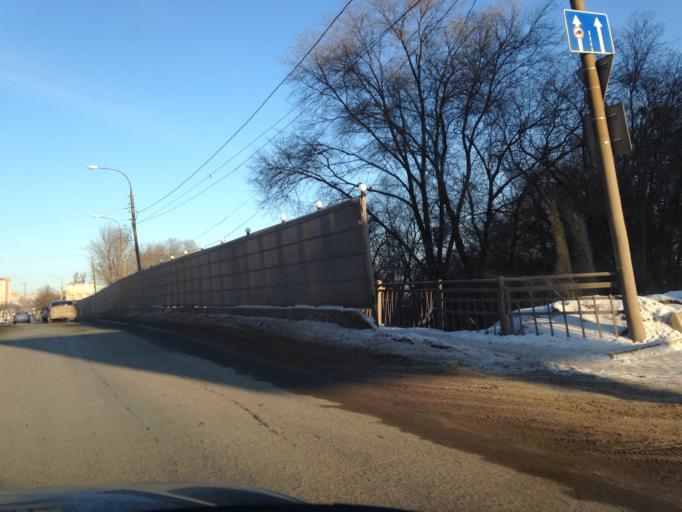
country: RU
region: Ulyanovsk
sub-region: Ulyanovskiy Rayon
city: Ulyanovsk
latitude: 54.2904
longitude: 48.3697
